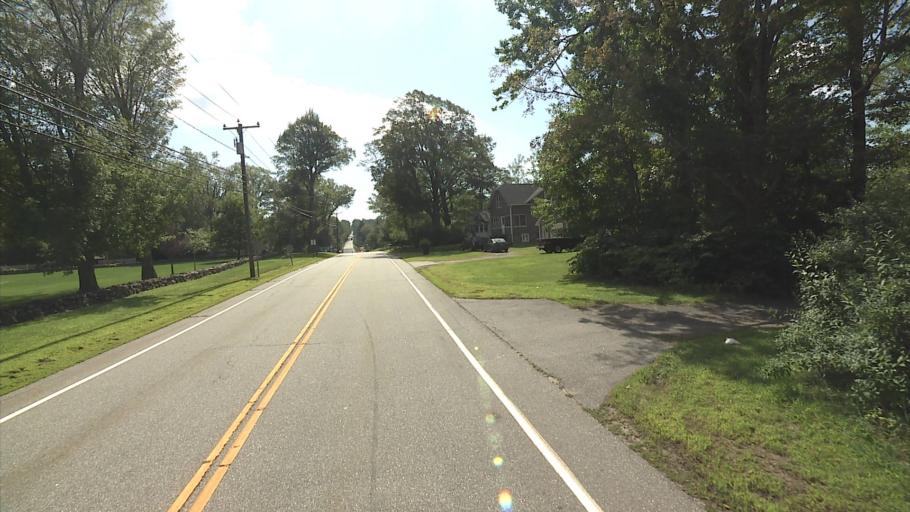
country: US
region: Connecticut
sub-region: Tolland County
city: Stafford Springs
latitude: 41.9574
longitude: -72.2853
